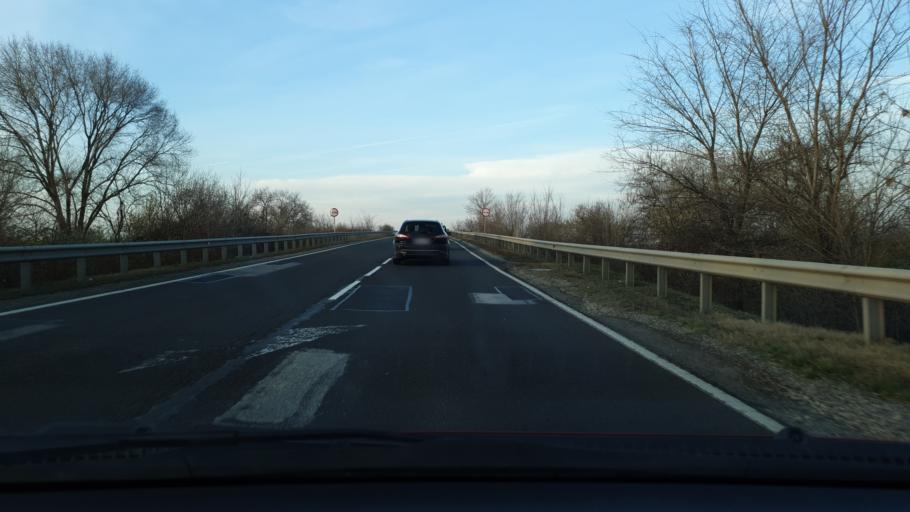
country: HU
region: Jasz-Nagykun-Szolnok
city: Toszeg
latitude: 47.1721
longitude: 20.1031
